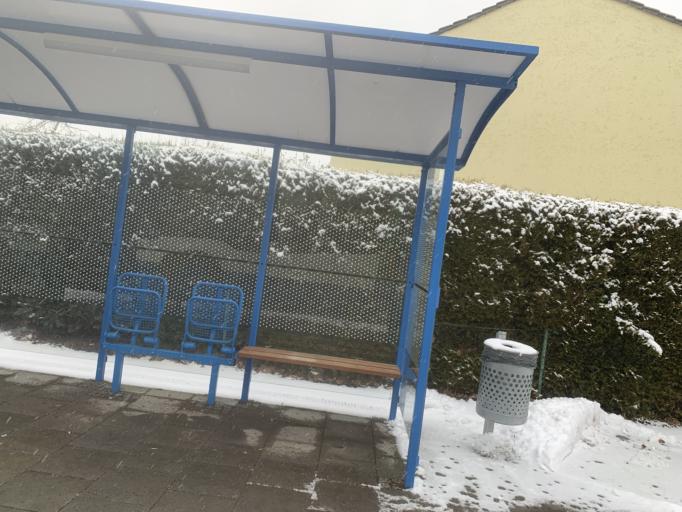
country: DE
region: Bavaria
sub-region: Upper Bavaria
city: Unterhaching
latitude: 48.0641
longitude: 11.6249
